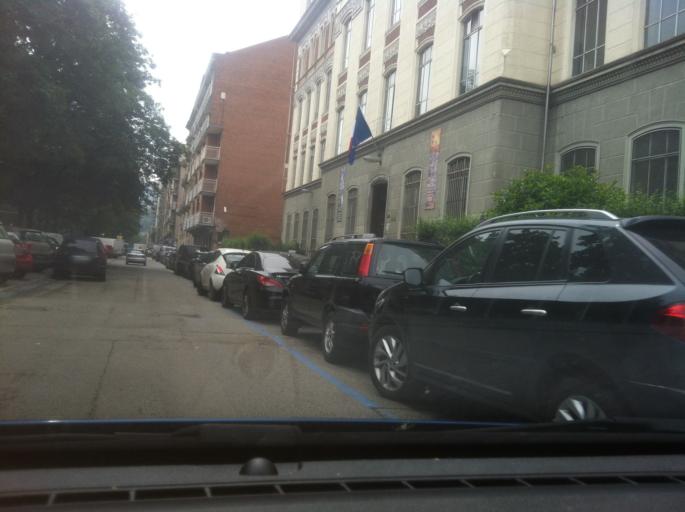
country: IT
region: Piedmont
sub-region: Provincia di Torino
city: Turin
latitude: 45.0713
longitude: 7.6928
